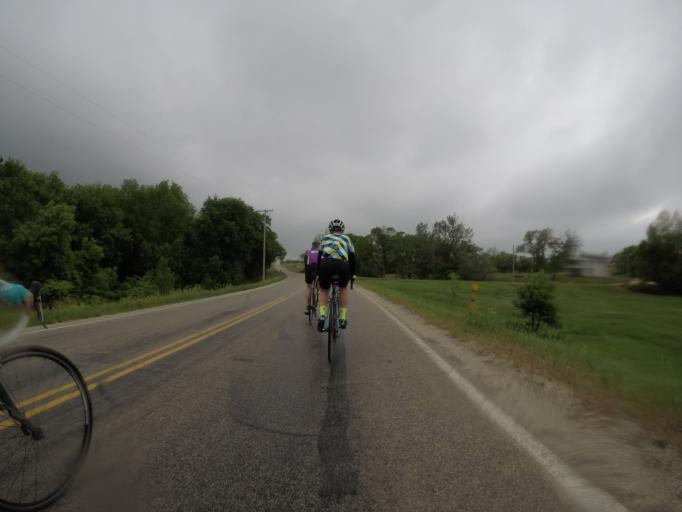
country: US
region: Kansas
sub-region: Pottawatomie County
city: Westmoreland
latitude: 39.4772
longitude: -96.1839
